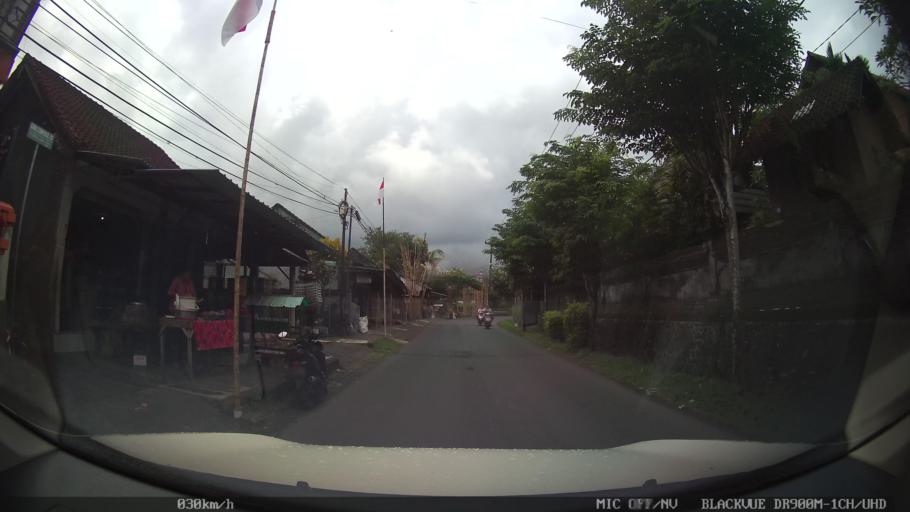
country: ID
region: Bali
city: Banjar Pekenjelodan
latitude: -8.5679
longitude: 115.1819
